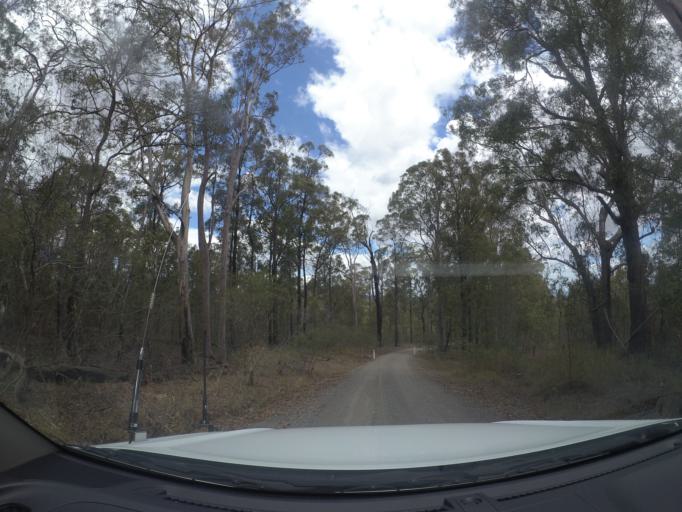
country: AU
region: Queensland
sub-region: Logan
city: Cedar Vale
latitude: -27.9036
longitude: 153.0320
